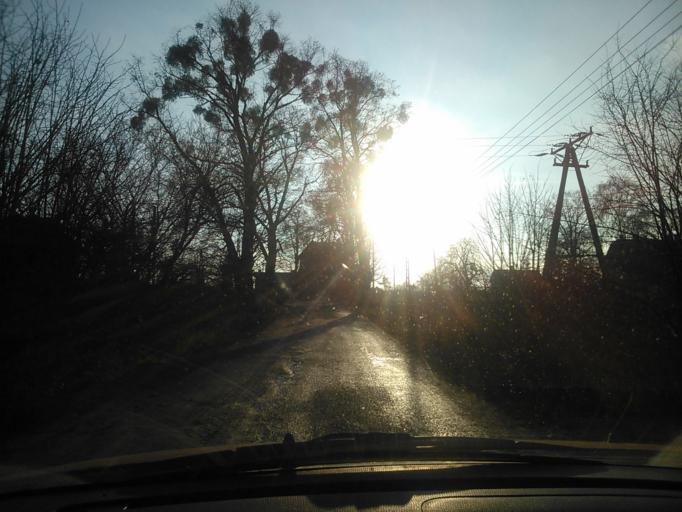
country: PL
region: Kujawsko-Pomorskie
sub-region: Powiat golubsko-dobrzynski
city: Golub-Dobrzyn
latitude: 53.1397
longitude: 18.9917
